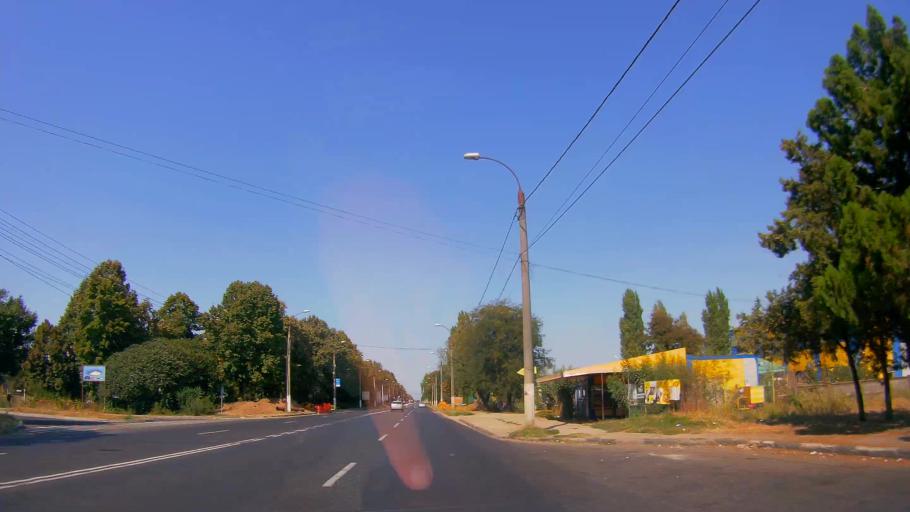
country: RO
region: Giurgiu
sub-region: Comuna Fratesti
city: Remus
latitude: 43.9218
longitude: 25.9736
